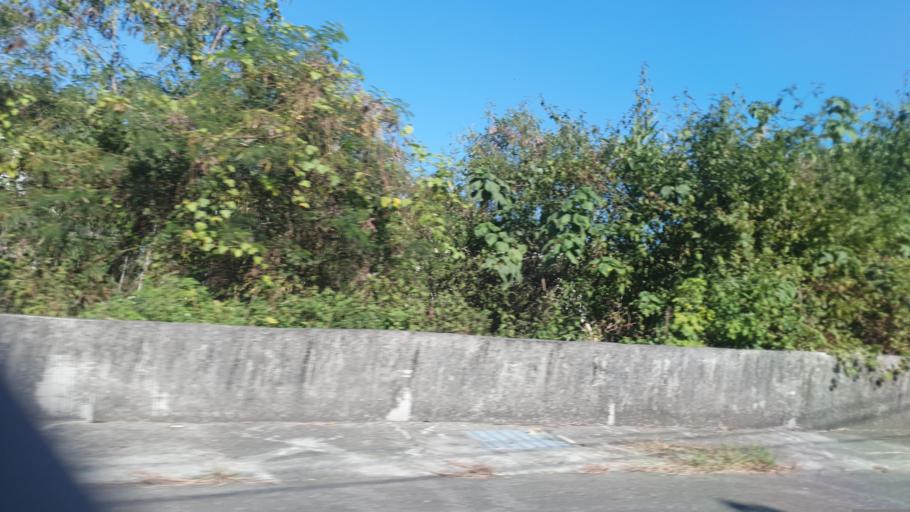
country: TW
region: Taiwan
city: Yujing
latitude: 23.0355
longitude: 120.3562
